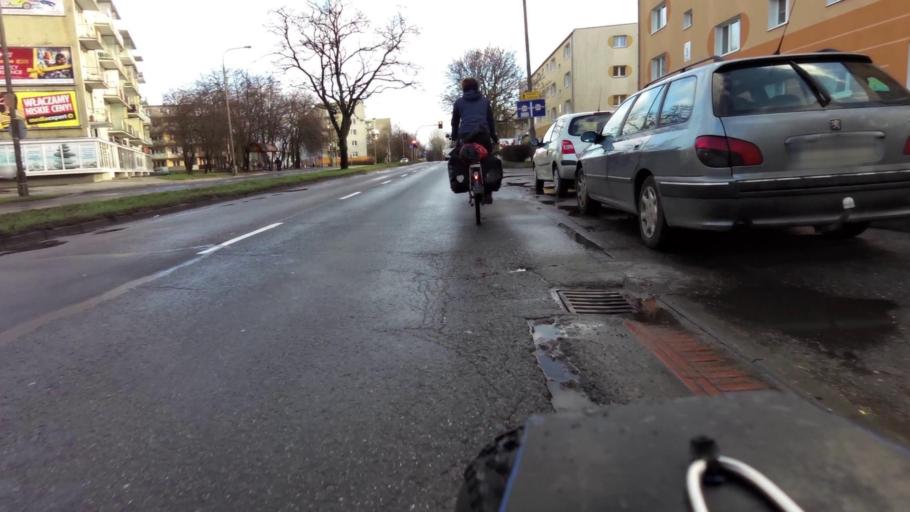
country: PL
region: Lubusz
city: Gorzow Wielkopolski
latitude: 52.7346
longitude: 15.2102
